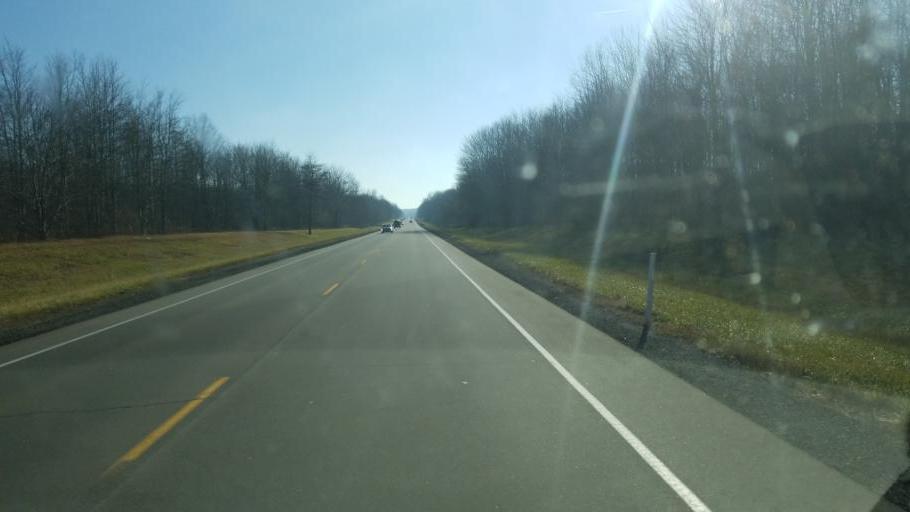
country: US
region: Ohio
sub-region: Lake County
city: Painesville
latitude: 41.6366
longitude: -81.2407
